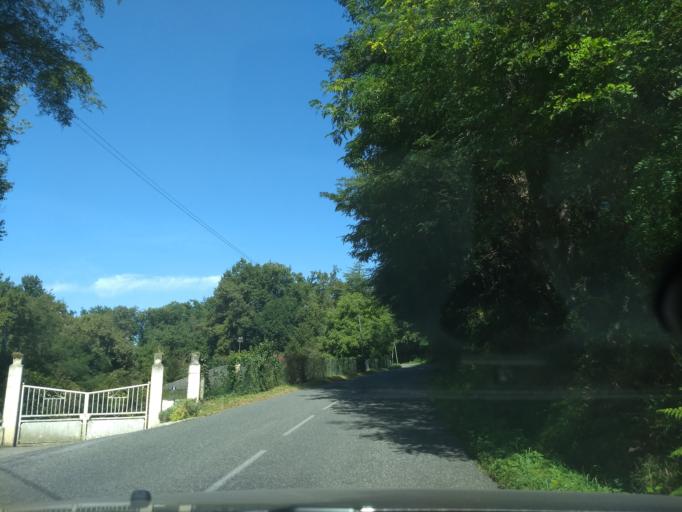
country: FR
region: Aquitaine
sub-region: Departement des Pyrenees-Atlantiques
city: Soumoulou
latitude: 43.2723
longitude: -0.1866
